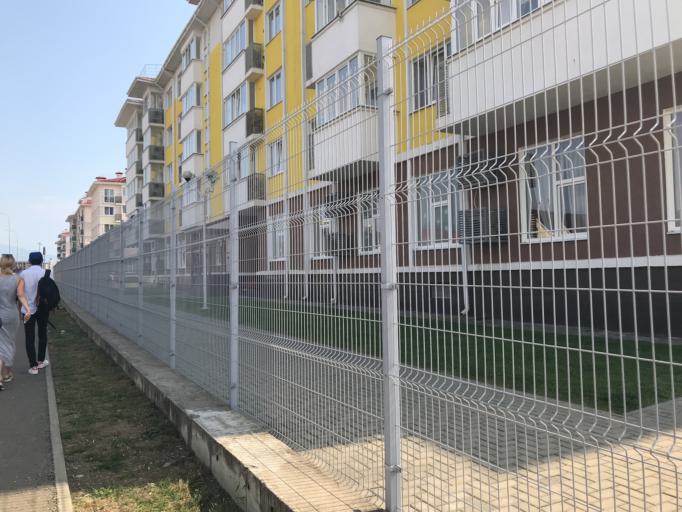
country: RU
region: Krasnodarskiy
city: Vysokoye
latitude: 43.4041
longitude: 39.9833
